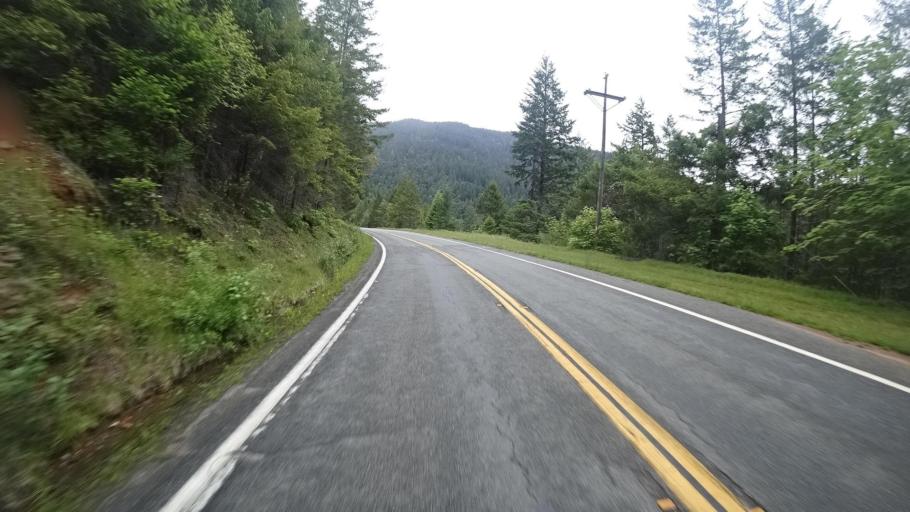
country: US
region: California
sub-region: Humboldt County
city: Willow Creek
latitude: 41.2700
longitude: -123.6059
